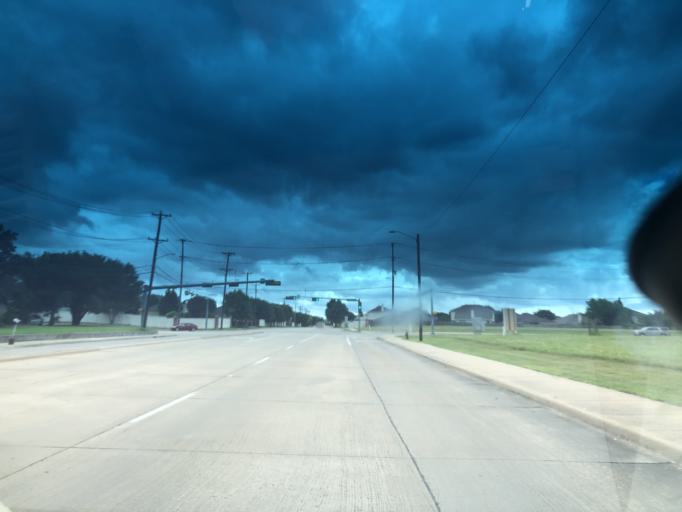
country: US
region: Texas
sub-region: Dallas County
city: Grand Prairie
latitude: 32.6974
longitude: -97.0182
